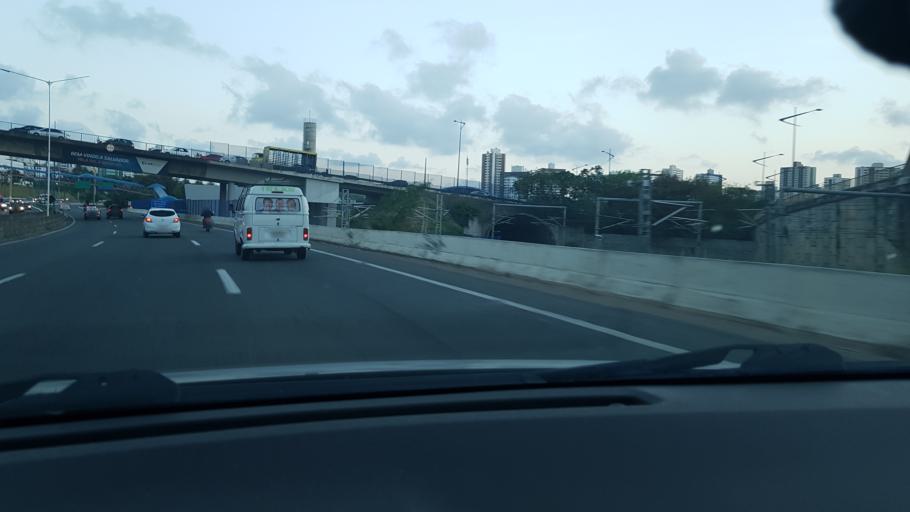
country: BR
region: Bahia
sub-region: Salvador
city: Salvador
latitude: -12.9669
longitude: -38.4771
